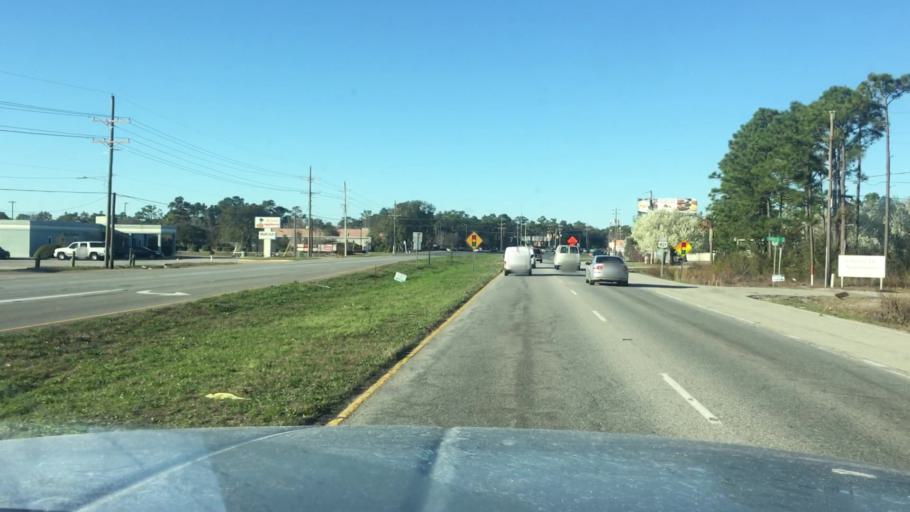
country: US
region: North Carolina
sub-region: New Hanover County
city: Myrtle Grove
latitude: 34.1227
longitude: -77.8999
